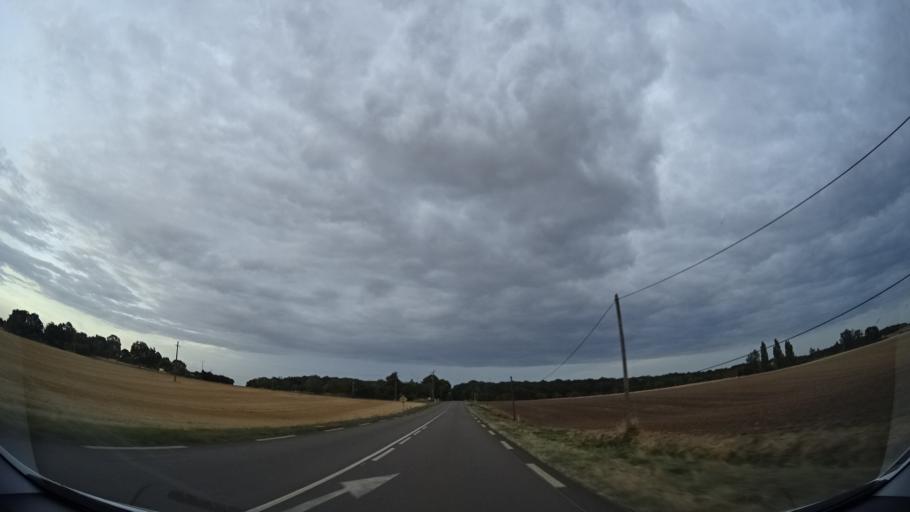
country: FR
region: Bourgogne
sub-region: Departement de l'Yonne
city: Charny
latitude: 47.9354
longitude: 3.1581
